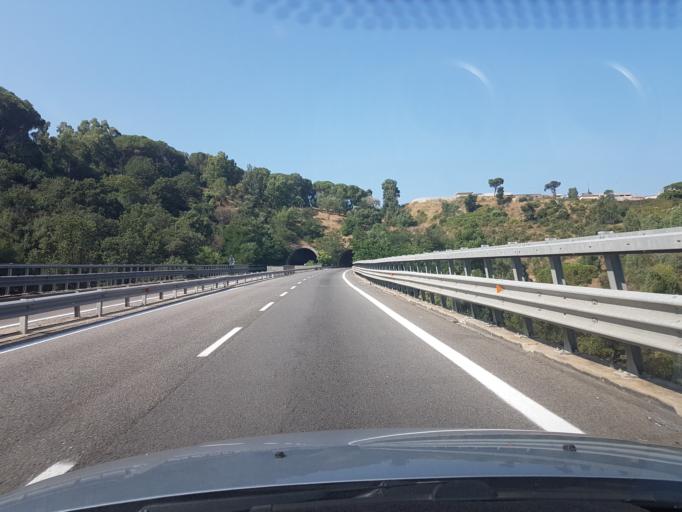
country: IT
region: Sardinia
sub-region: Provincia di Nuoro
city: Nuoro
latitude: 40.3311
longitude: 9.2922
